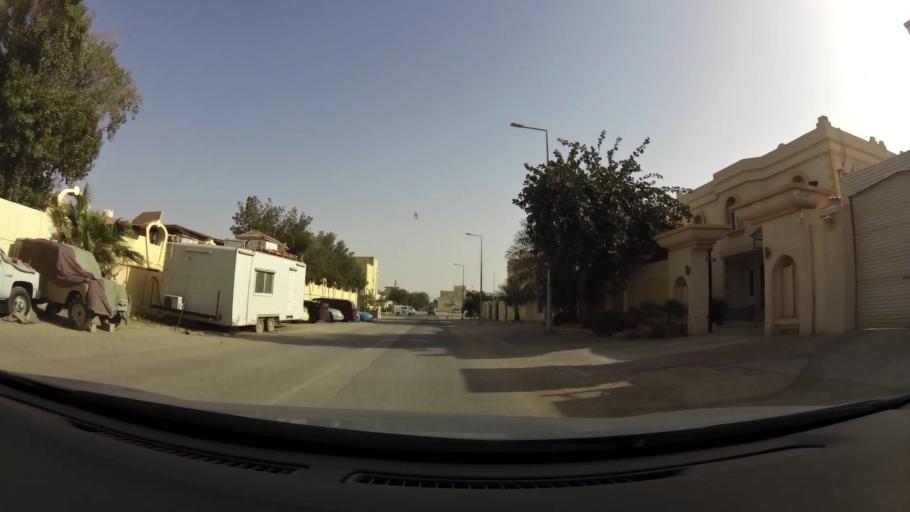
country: QA
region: Baladiyat ar Rayyan
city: Ar Rayyan
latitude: 25.3380
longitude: 51.4443
